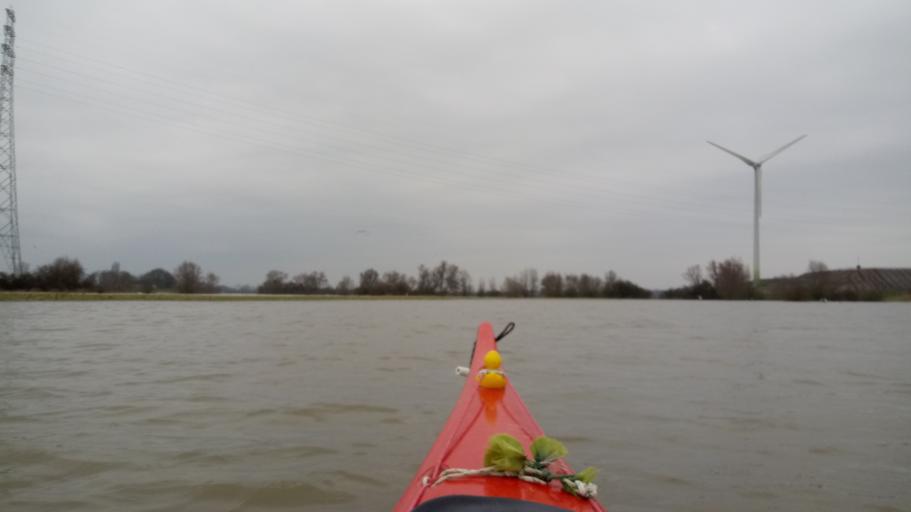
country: NL
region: Gelderland
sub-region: Gemeente Zutphen
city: Zutphen
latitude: 52.1605
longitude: 6.1882
